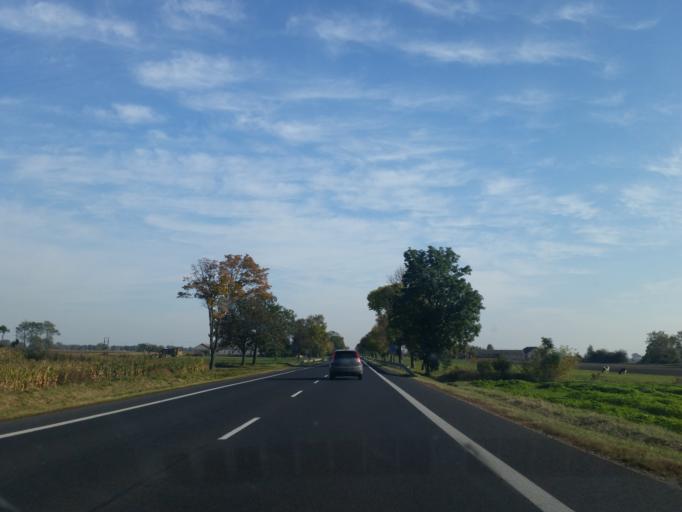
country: PL
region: Masovian Voivodeship
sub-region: Powiat plocki
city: Drobin
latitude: 52.7642
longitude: 19.9428
